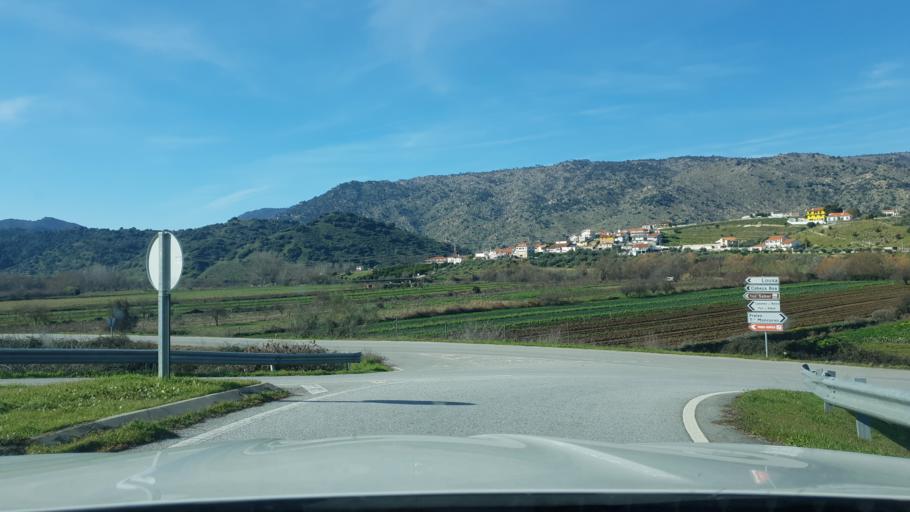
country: PT
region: Braganca
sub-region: Torre de Moncorvo
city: Torre de Moncorvo
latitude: 41.1811
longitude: -7.1035
